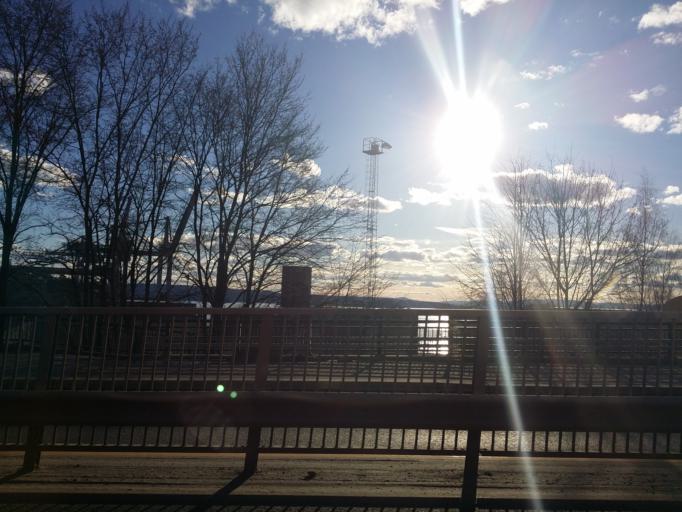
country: NO
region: Oslo
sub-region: Oslo
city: Oslo
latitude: 59.8842
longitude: 10.7692
